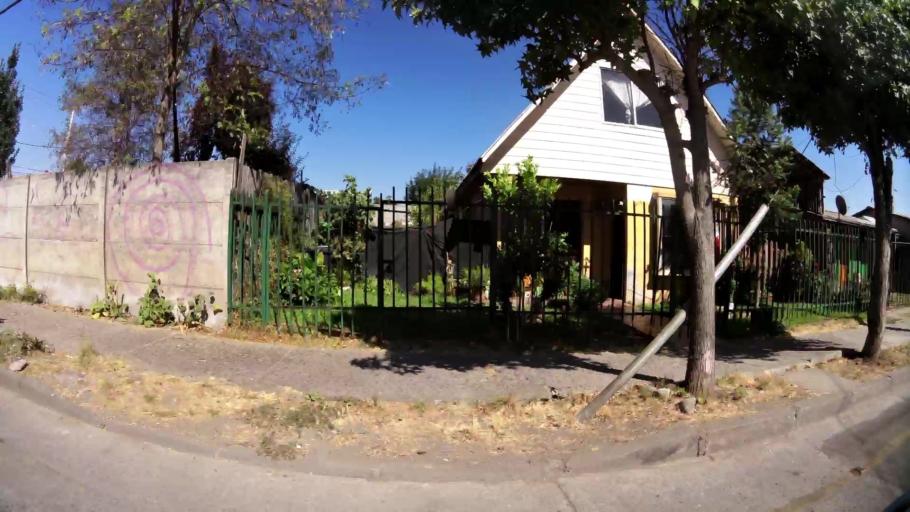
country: CL
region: Maule
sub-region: Provincia de Curico
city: Curico
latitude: -34.9746
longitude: -71.2551
